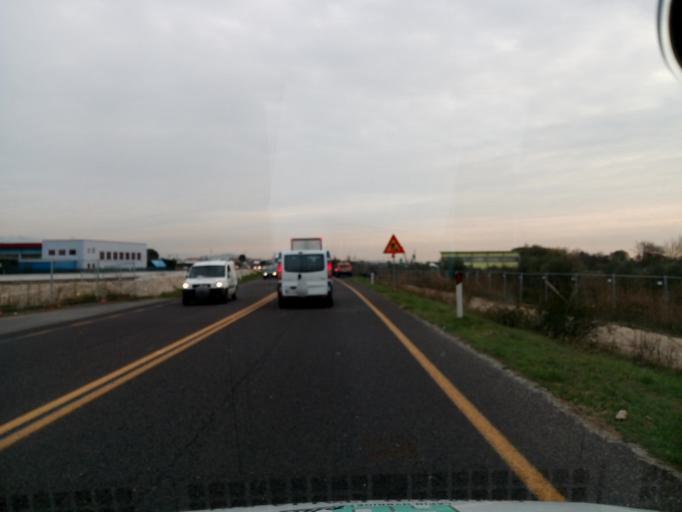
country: IT
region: Veneto
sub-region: Provincia di Vicenza
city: San Zeno-San Giuseppe
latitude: 45.7385
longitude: 11.7700
